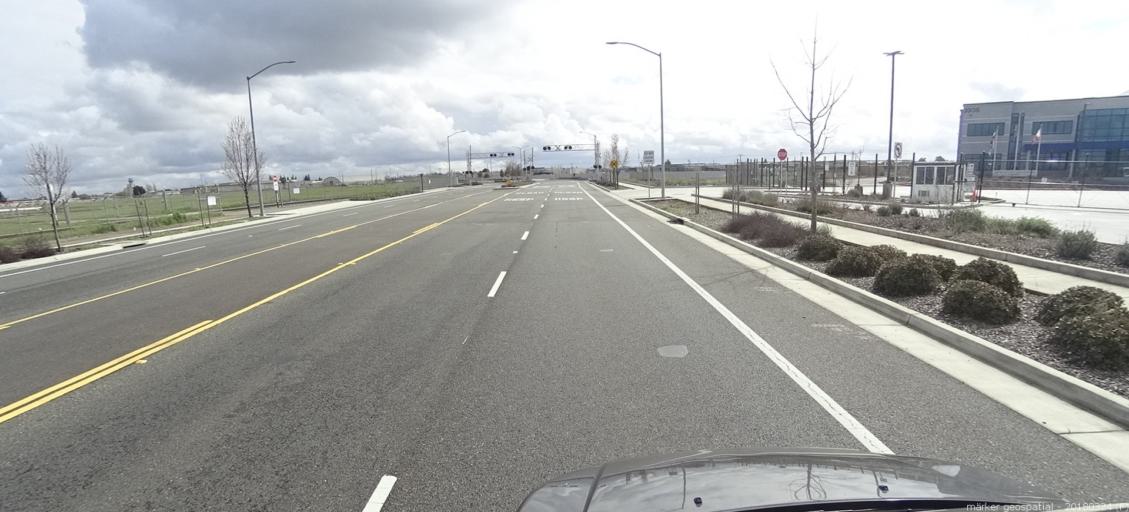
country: US
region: California
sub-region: Sacramento County
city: North Highlands
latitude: 38.6469
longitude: -121.4019
